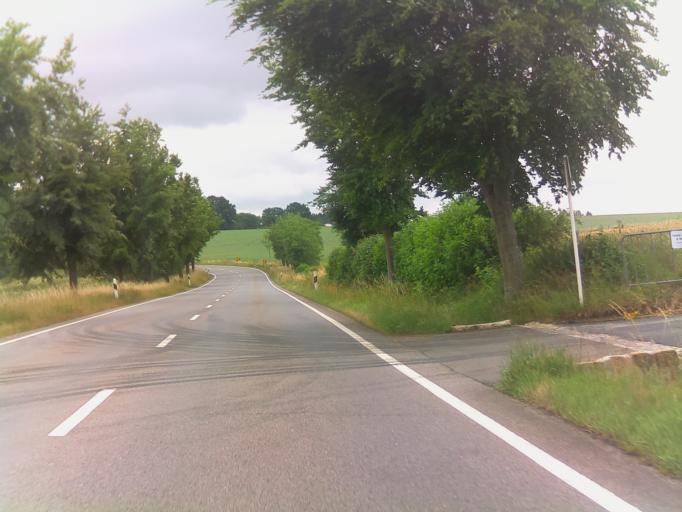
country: LU
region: Luxembourg
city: Schouweiler
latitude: 49.5916
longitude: 5.9613
